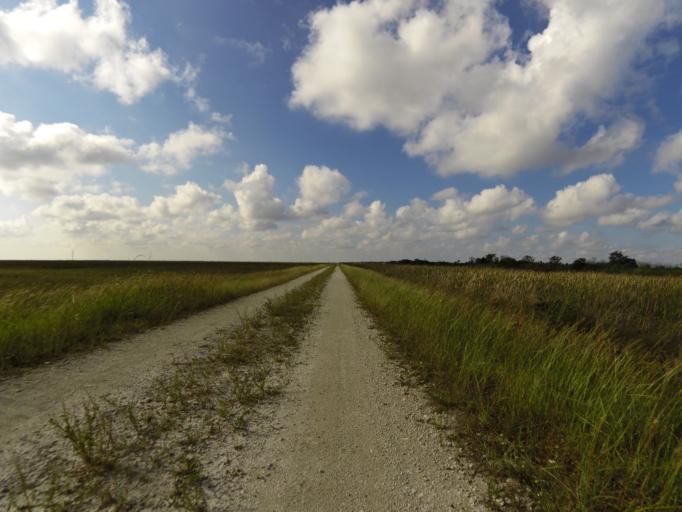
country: US
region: Florida
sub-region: Broward County
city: Weston
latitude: 26.0448
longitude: -80.4847
